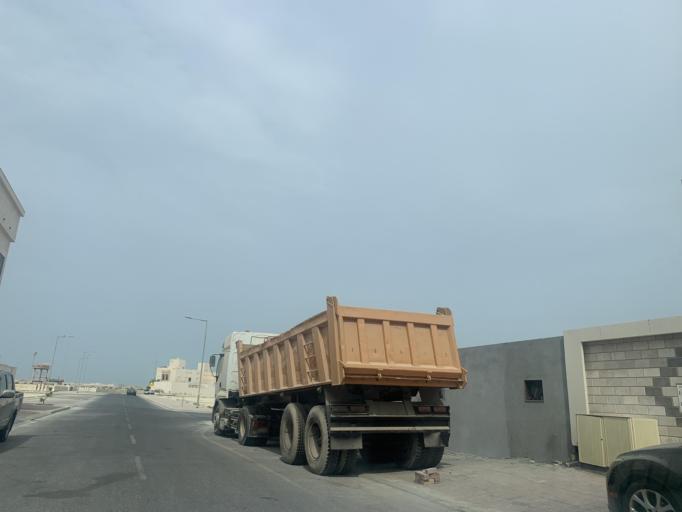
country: BH
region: Muharraq
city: Al Muharraq
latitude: 26.2862
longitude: 50.6360
